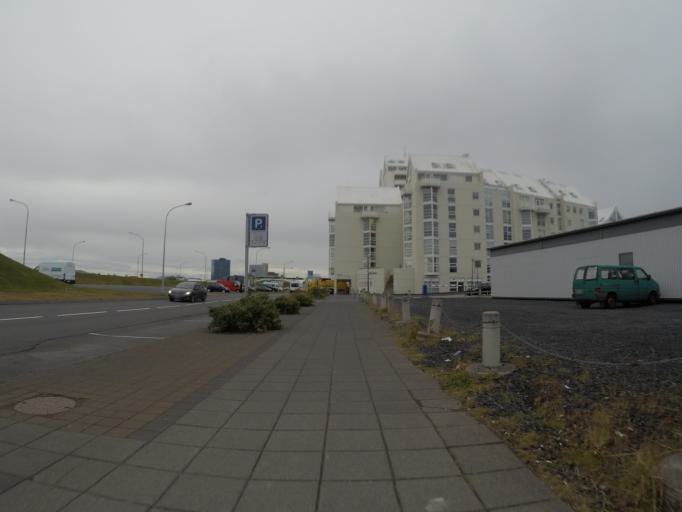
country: IS
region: Capital Region
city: Reykjavik
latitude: 64.1484
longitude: -21.9283
